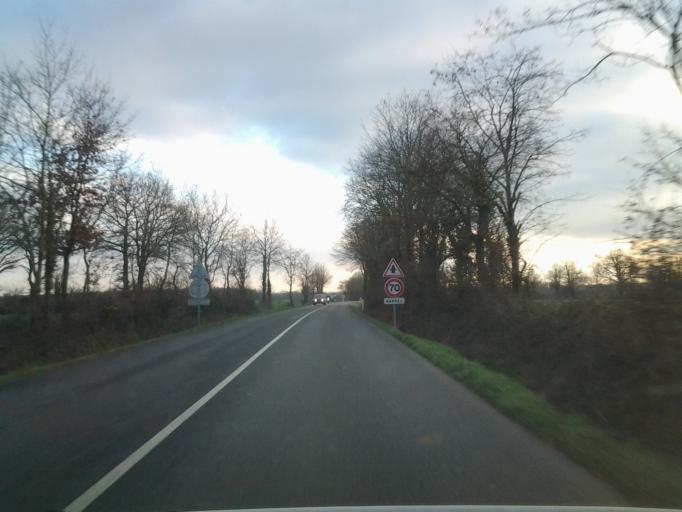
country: FR
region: Pays de la Loire
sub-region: Departement de la Vendee
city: Mouilleron-le-Captif
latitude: 46.7078
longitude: -1.4156
